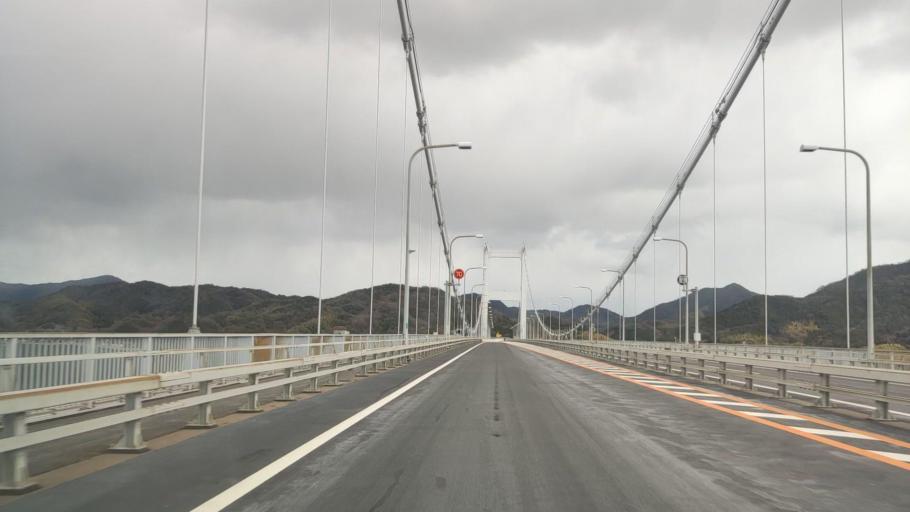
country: JP
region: Hiroshima
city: Takehara
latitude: 34.1251
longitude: 133.0101
